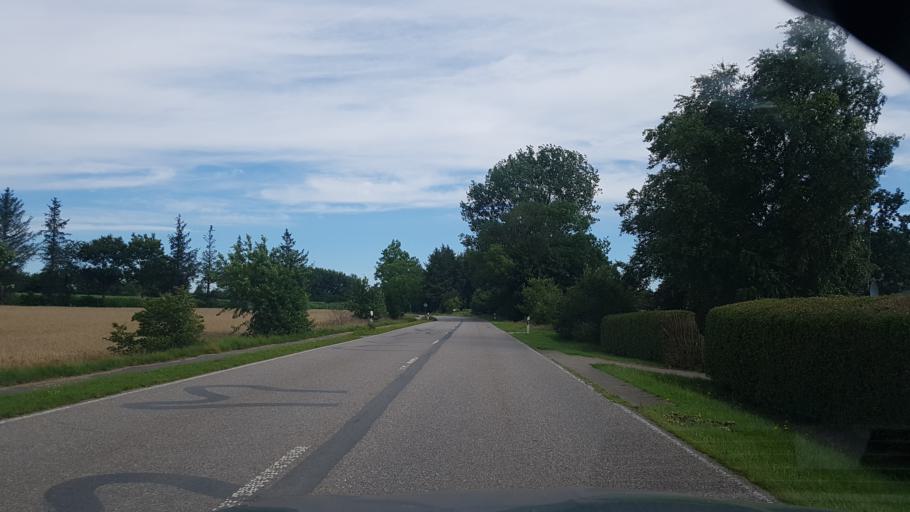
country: DE
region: Schleswig-Holstein
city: Ladelund
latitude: 54.8456
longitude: 9.0353
